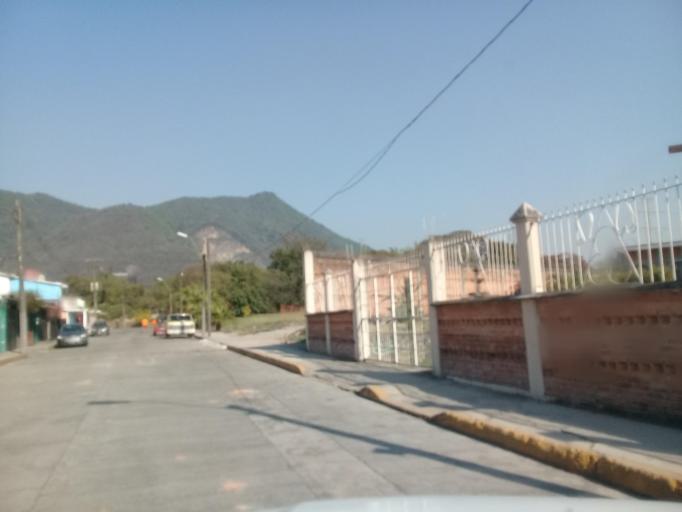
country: MX
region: Veracruz
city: Ixtac Zoquitlan
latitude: 18.8575
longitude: -97.0661
